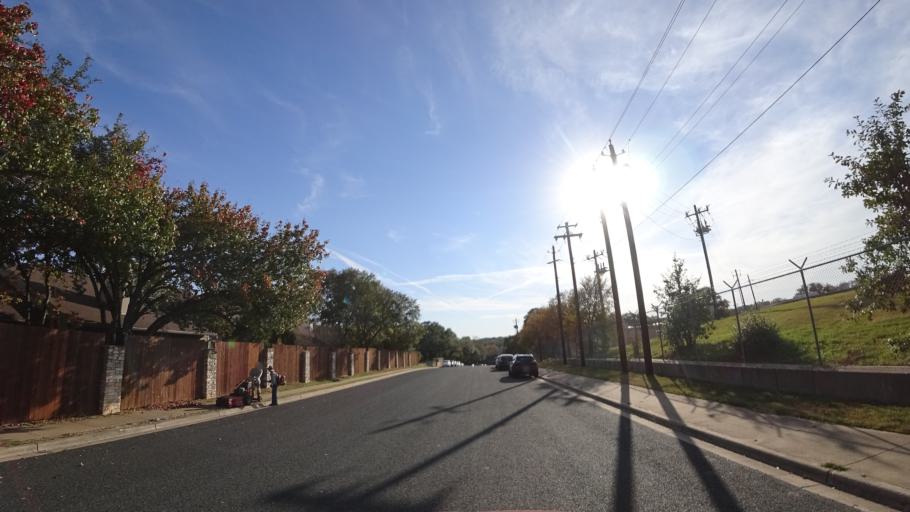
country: US
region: Texas
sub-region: Williamson County
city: Jollyville
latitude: 30.3718
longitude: -97.7542
